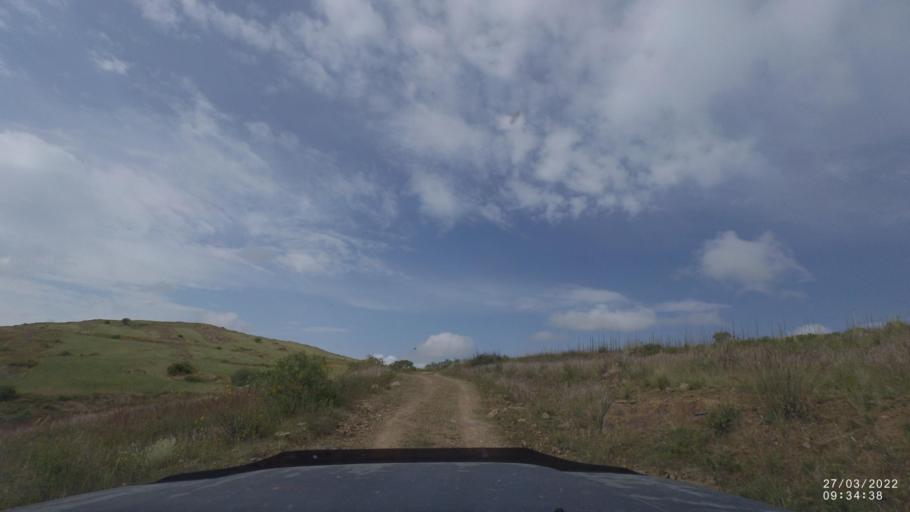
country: BO
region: Cochabamba
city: Cliza
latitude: -17.7433
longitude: -65.8910
